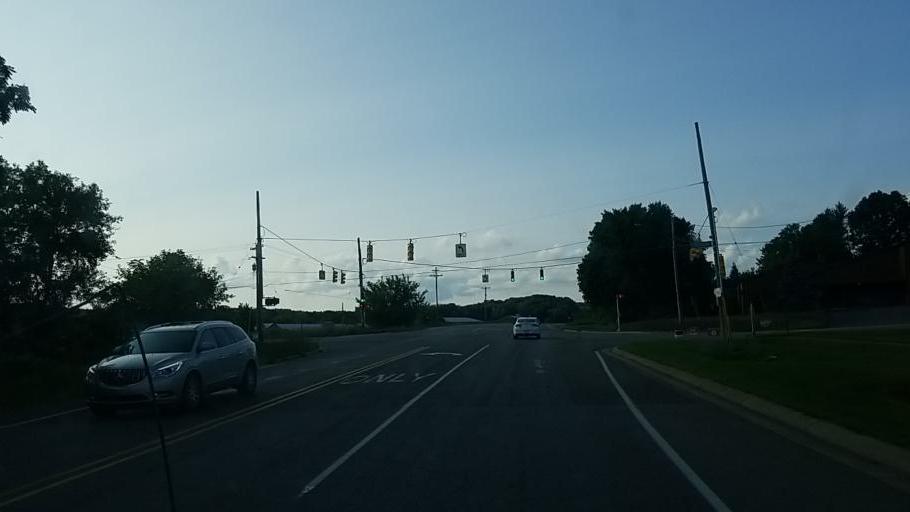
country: US
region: Michigan
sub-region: Kent County
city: Lowell
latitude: 42.9580
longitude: -85.3549
